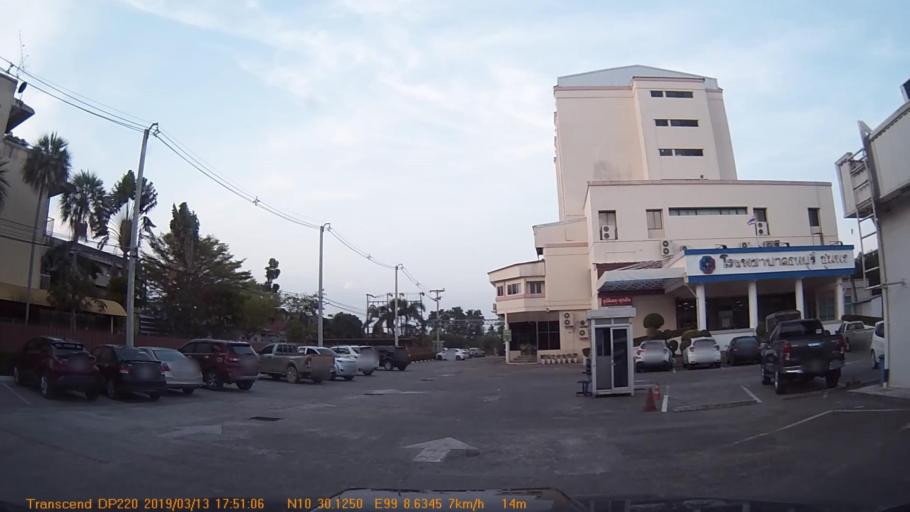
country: TH
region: Chumphon
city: Chumphon
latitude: 10.5002
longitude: 99.1422
